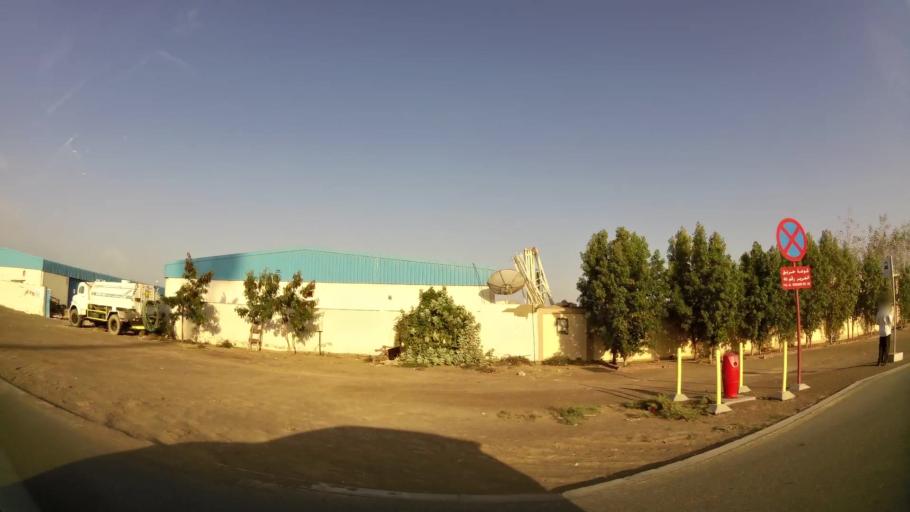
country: AE
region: Abu Dhabi
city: Al Ain
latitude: 24.1459
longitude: 55.8419
